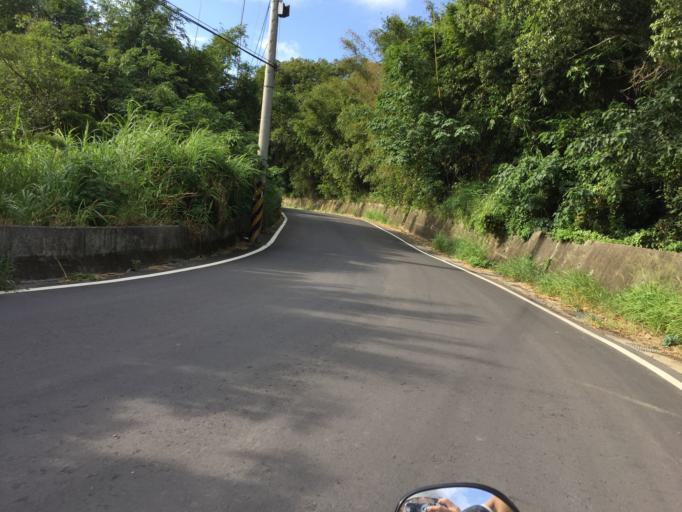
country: TW
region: Taiwan
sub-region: Hsinchu
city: Hsinchu
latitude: 24.7708
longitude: 120.9374
